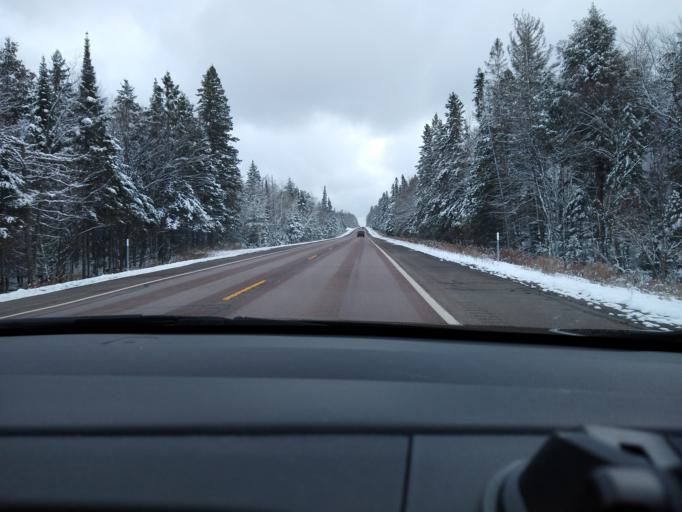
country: US
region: Wisconsin
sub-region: Vilas County
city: Eagle River
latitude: 46.2256
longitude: -89.0667
